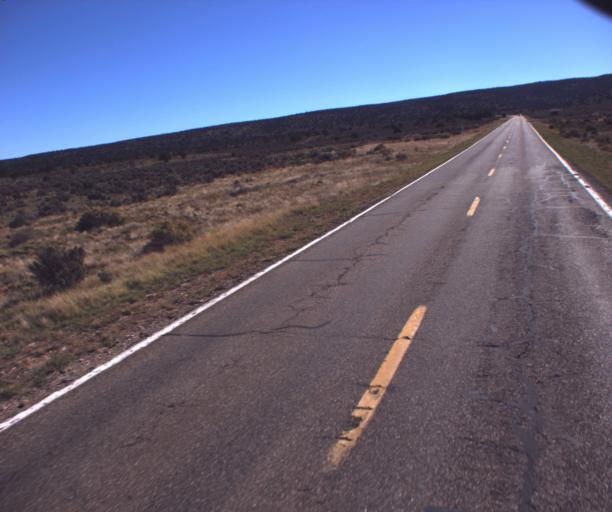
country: US
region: Arizona
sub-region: Coconino County
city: Fredonia
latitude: 36.8500
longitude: -112.2879
